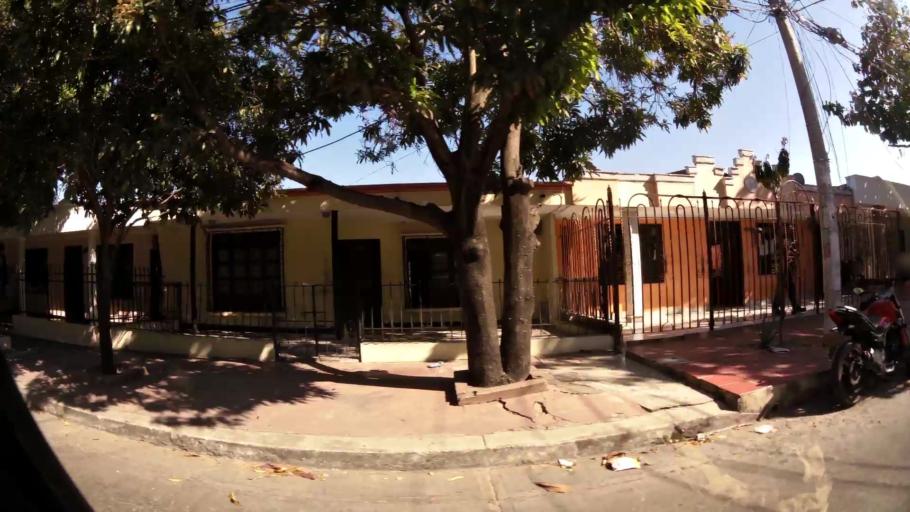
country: CO
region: Atlantico
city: Barranquilla
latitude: 10.9493
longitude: -74.7922
